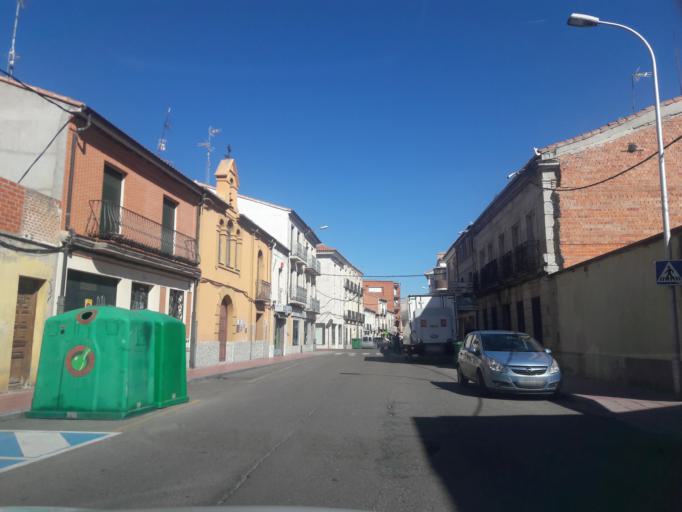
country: ES
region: Castille and Leon
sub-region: Provincia de Salamanca
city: Penaranda de Bracamonte
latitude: 40.9001
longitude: -5.2012
